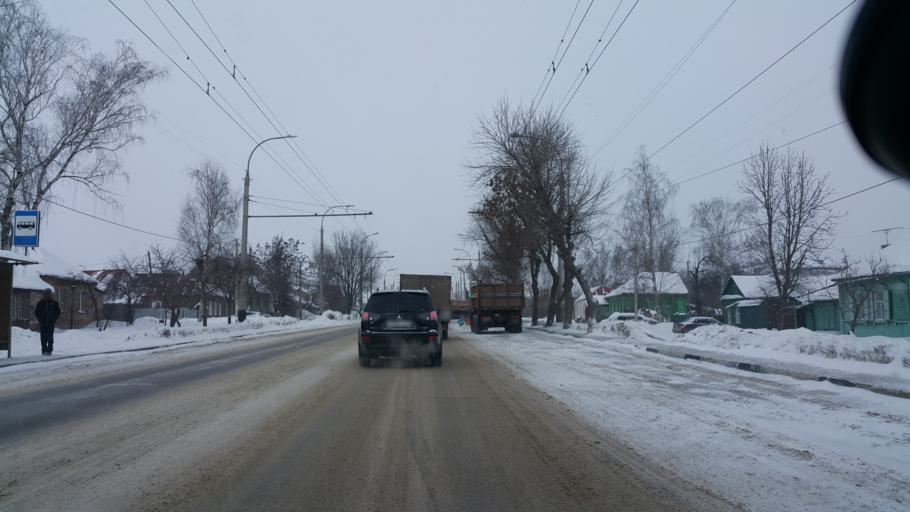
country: RU
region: Tambov
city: Tambov
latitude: 52.7232
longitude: 41.4037
